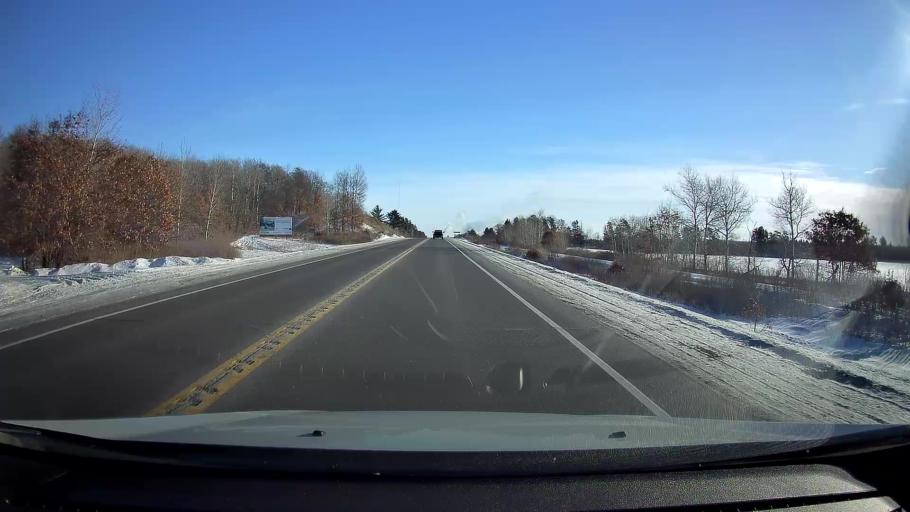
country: US
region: Wisconsin
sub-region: Sawyer County
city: Hayward
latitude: 45.9819
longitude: -91.5560
